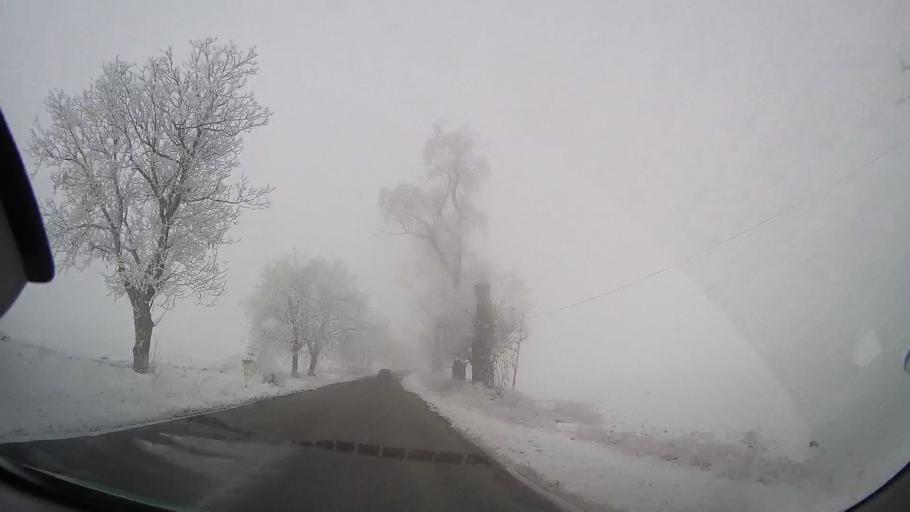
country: RO
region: Neamt
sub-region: Comuna Sabaoani
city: Sabaoani
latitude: 46.9874
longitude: 26.8633
